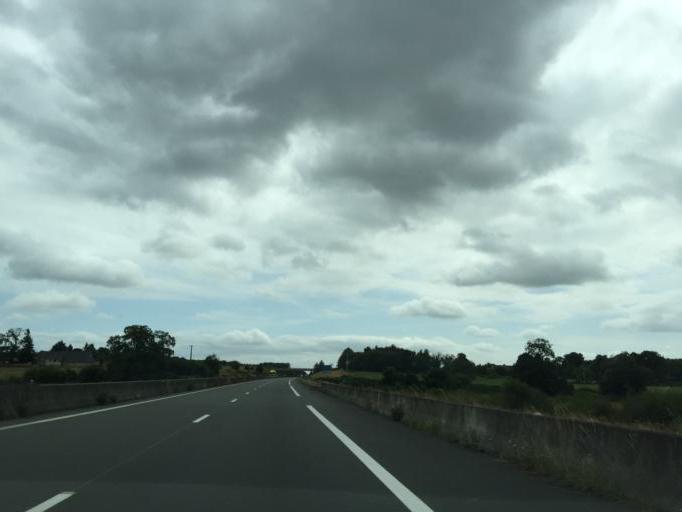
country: FR
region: Pays de la Loire
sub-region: Departement de la Sarthe
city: Mayet
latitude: 47.7721
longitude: 0.3137
